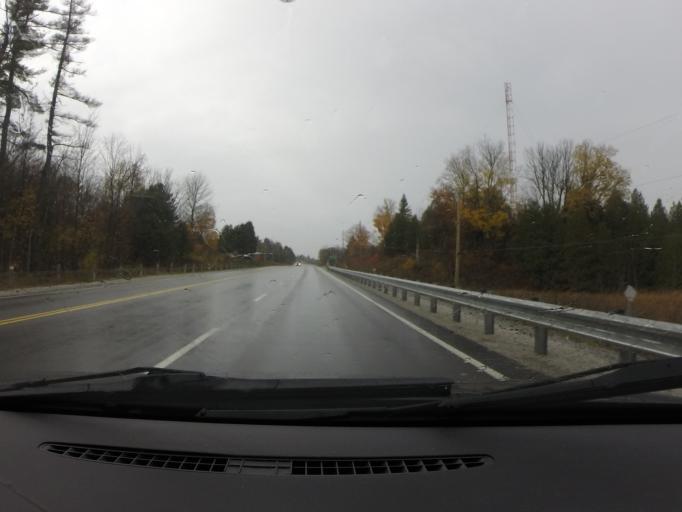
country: CA
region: Ontario
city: Perth
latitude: 44.8493
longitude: -76.4736
